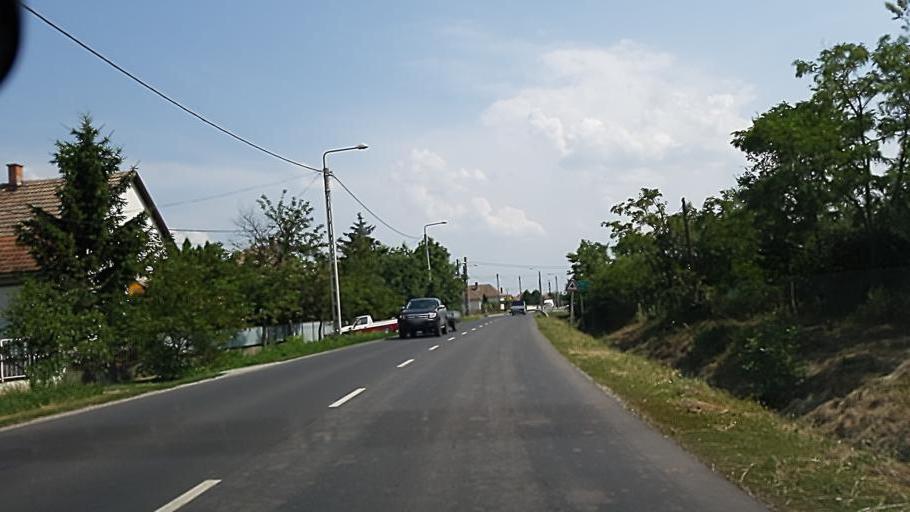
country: HU
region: Heves
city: Poroszlo
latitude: 47.6427
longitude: 20.6392
